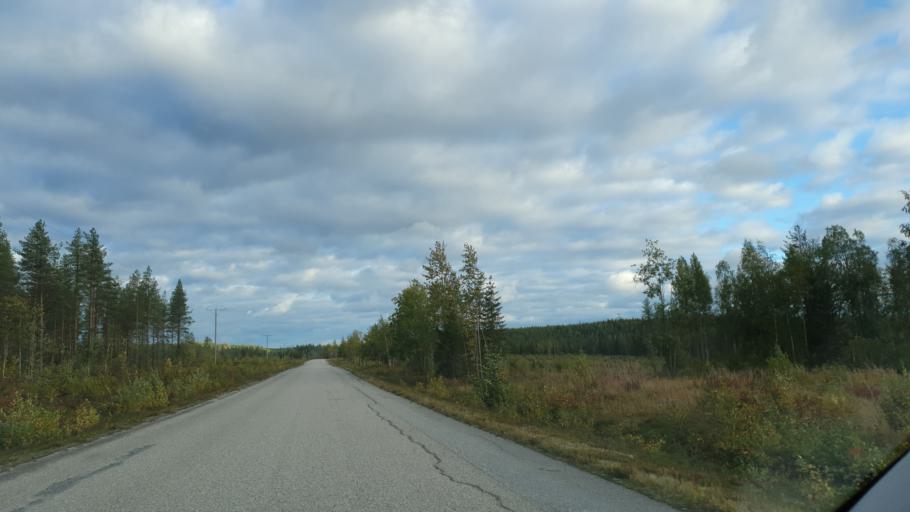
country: FI
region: North Karelia
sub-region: Pielisen Karjala
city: Lieksa
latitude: 63.9192
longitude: 30.1624
